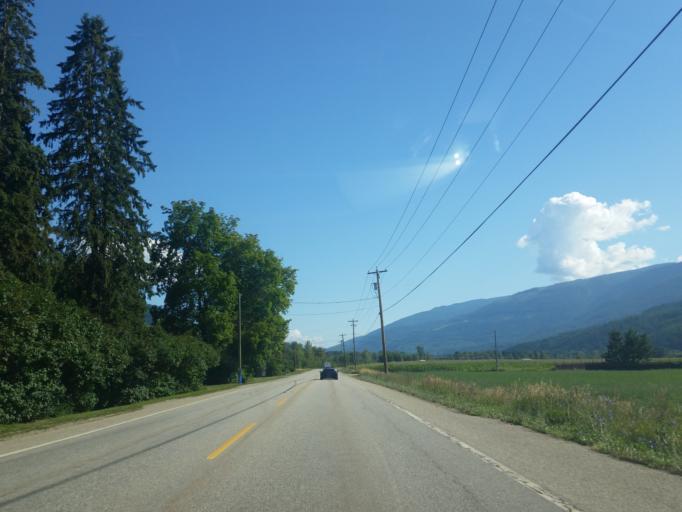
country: CA
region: British Columbia
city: Enderby
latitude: 50.6388
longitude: -119.1063
